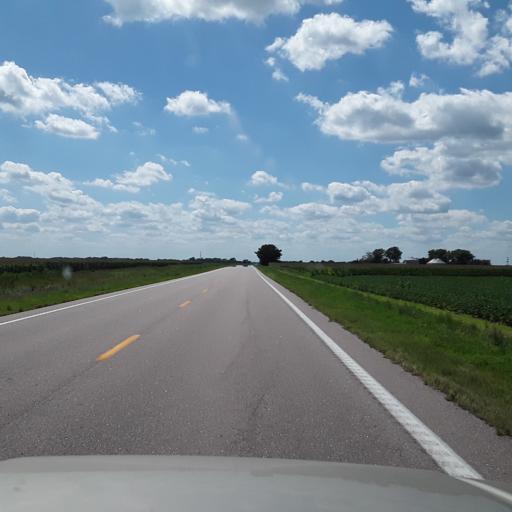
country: US
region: Nebraska
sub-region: Merrick County
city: Central City
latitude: 41.1914
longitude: -98.0713
